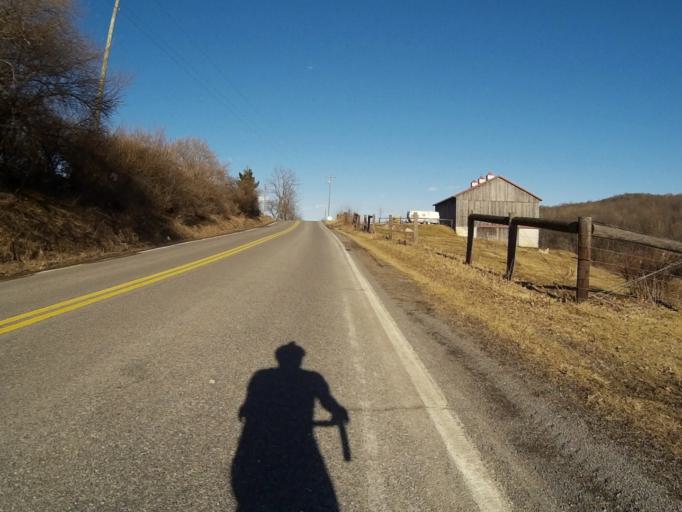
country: US
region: Pennsylvania
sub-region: Centre County
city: Park Forest Village
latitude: 40.8435
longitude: -77.9148
